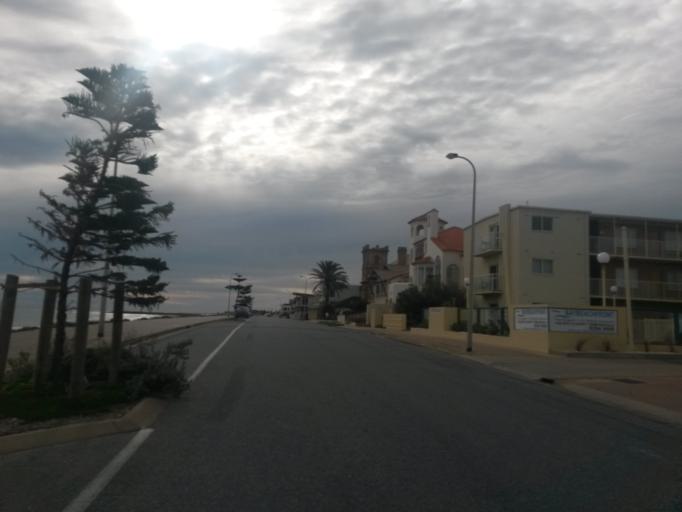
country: AU
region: South Australia
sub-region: Adelaide
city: Glenelg
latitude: -34.9687
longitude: 138.5103
